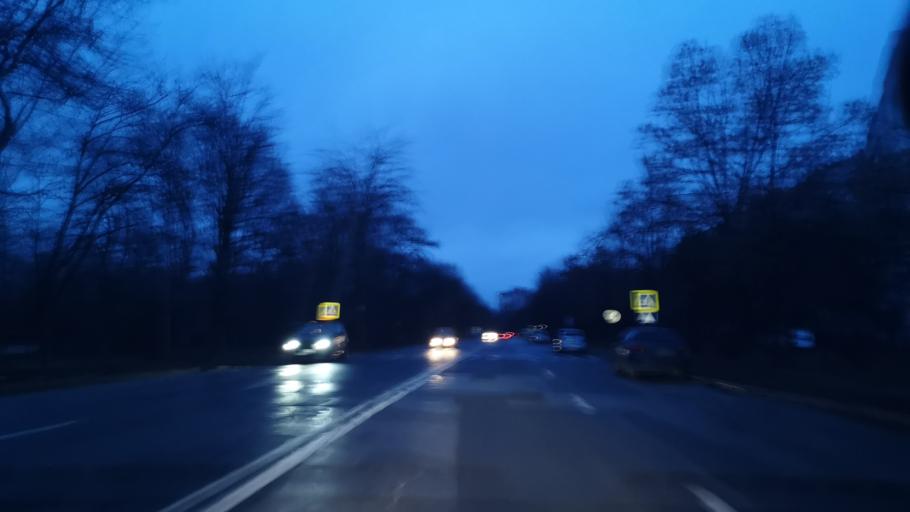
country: MD
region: Chisinau
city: Chisinau
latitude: 47.0350
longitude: 28.8783
